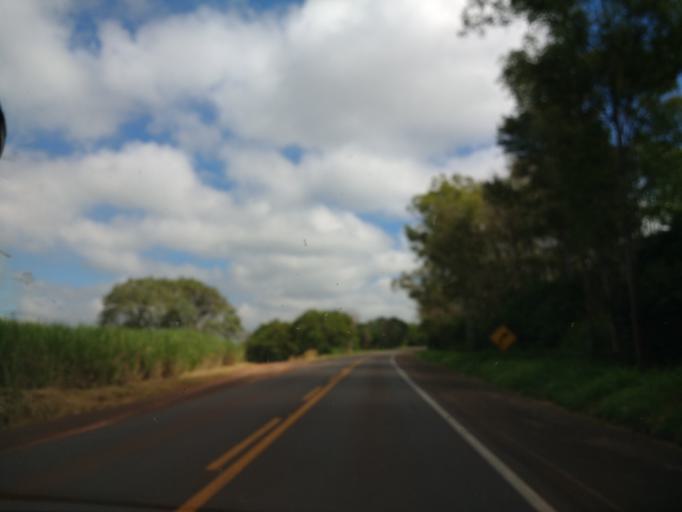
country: BR
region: Parana
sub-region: Cruzeiro Do Oeste
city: Cruzeiro do Oeste
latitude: -23.7635
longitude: -52.9858
